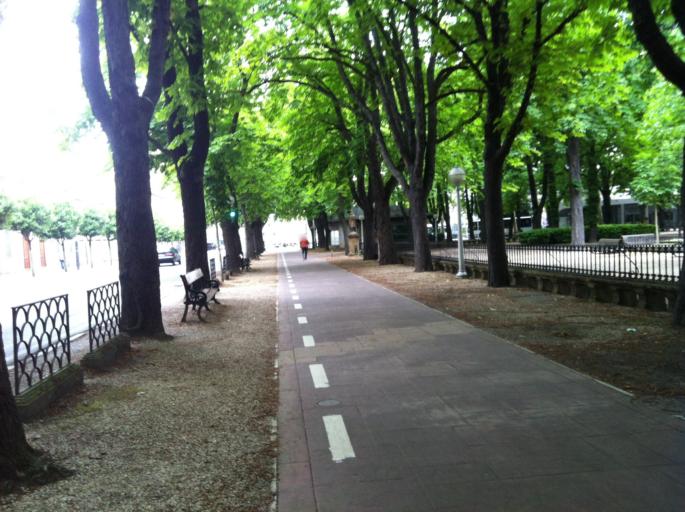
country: ES
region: Basque Country
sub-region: Provincia de Alava
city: Gasteiz / Vitoria
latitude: 42.8436
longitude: -2.6770
